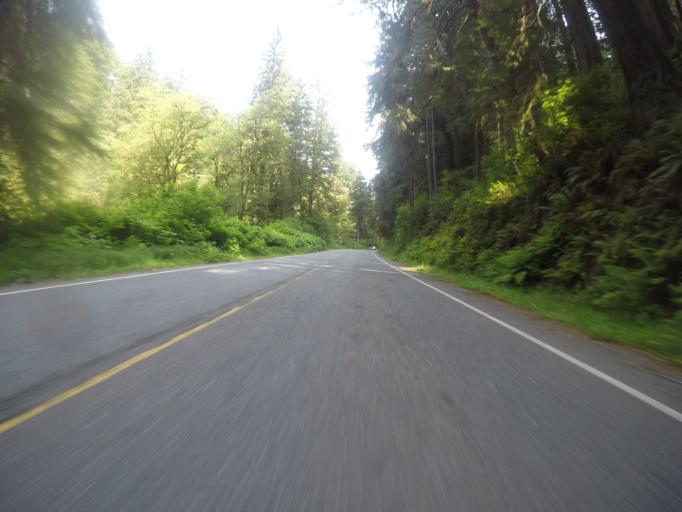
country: US
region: California
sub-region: Del Norte County
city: Bertsch-Oceanview
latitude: 41.4307
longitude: -124.0381
